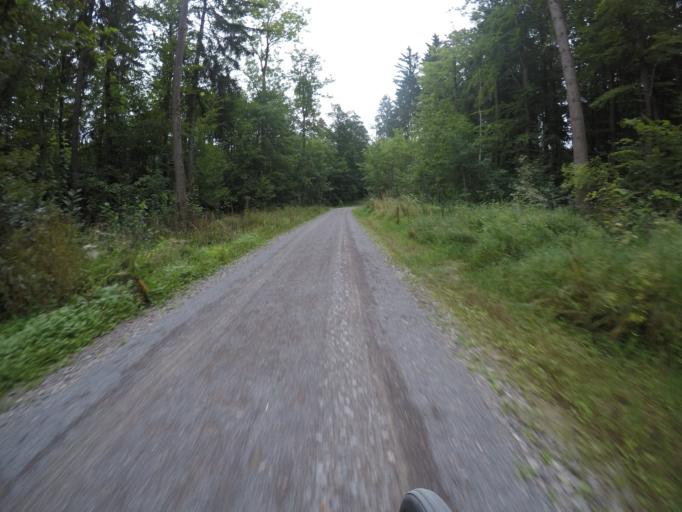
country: DE
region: Baden-Wuerttemberg
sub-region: Regierungsbezirk Stuttgart
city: Boeblingen
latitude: 48.6655
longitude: 9.0289
